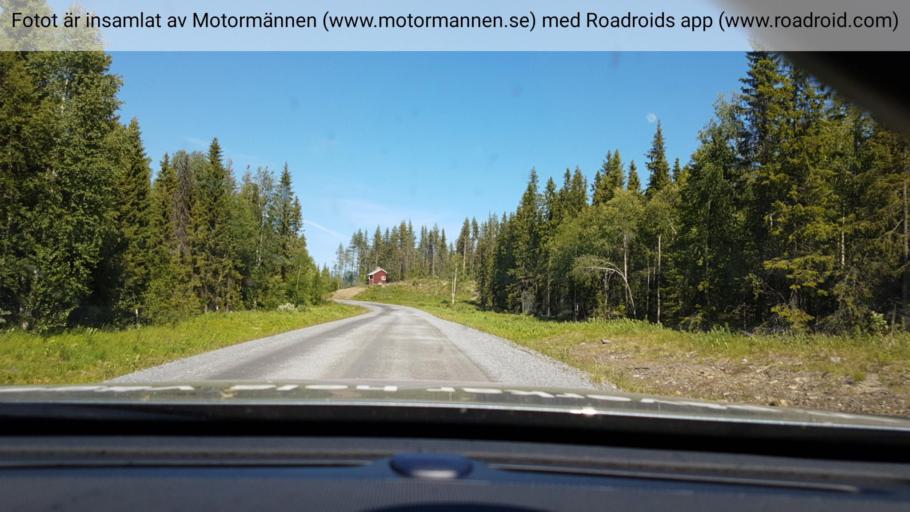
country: SE
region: Vaesterbotten
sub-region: Vilhelmina Kommun
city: Sjoberg
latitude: 64.6855
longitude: 15.7543
